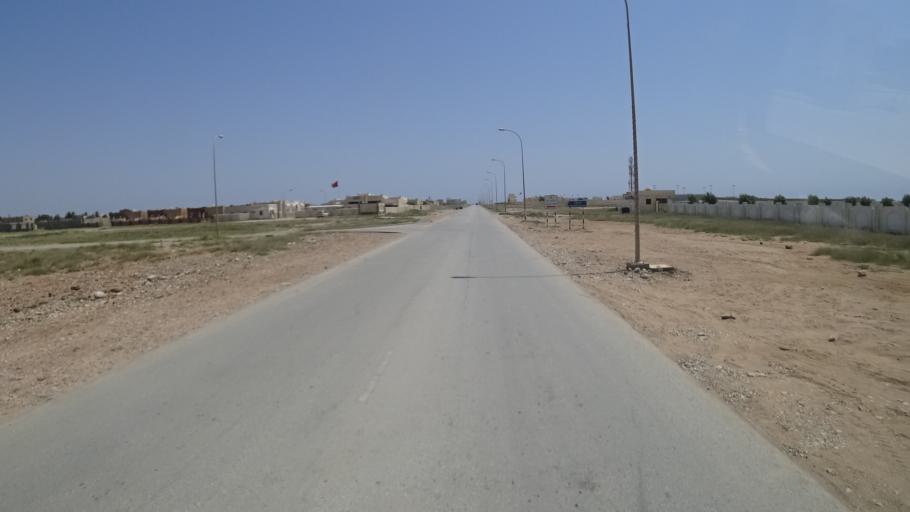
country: OM
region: Zufar
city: Salalah
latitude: 16.9873
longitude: 54.6973
